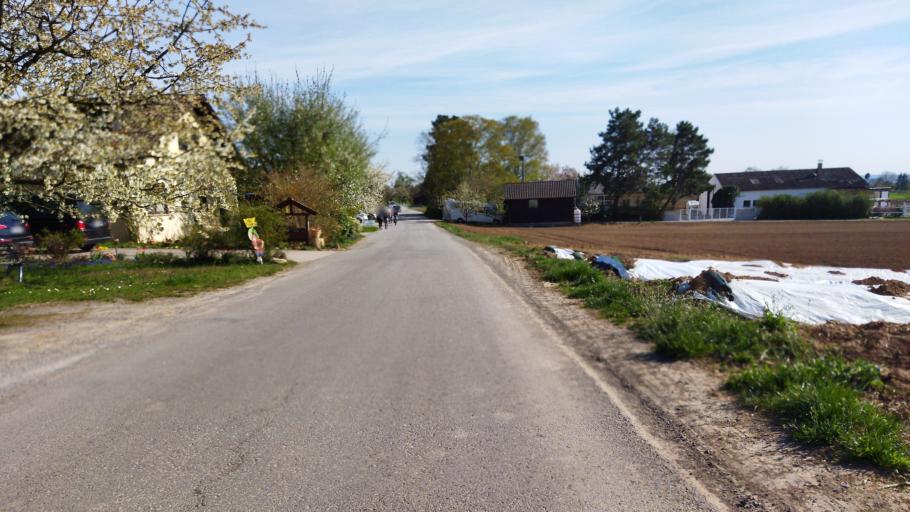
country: DE
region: Baden-Wuerttemberg
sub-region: Regierungsbezirk Stuttgart
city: Freudental
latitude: 48.9777
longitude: 9.0664
